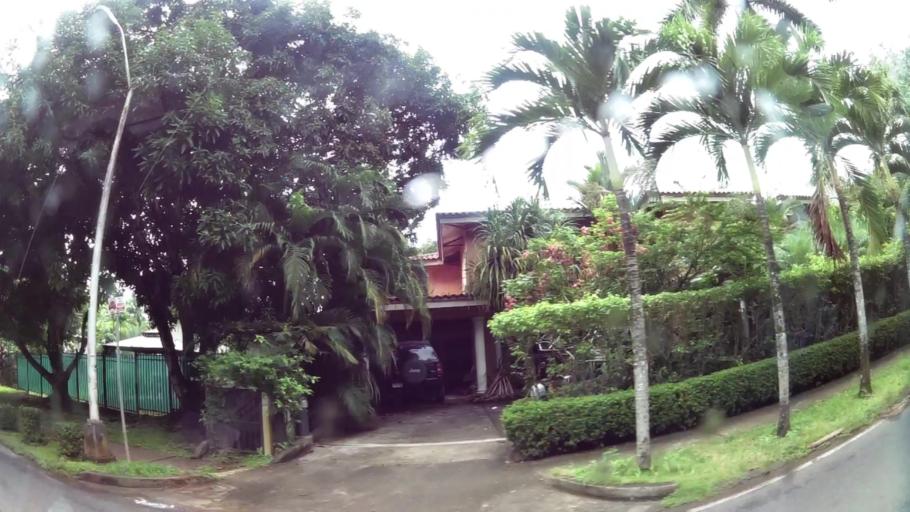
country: PA
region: Panama
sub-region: Distrito de Panama
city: Ancon
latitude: 9.0062
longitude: -79.5758
